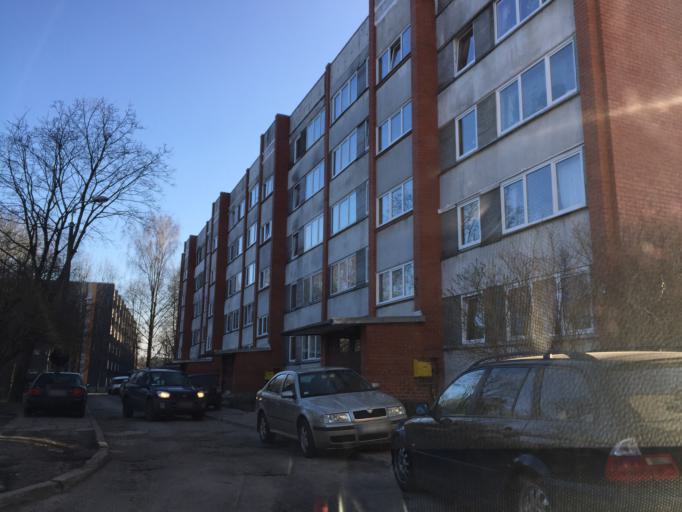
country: LV
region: Riga
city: Bergi
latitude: 56.9772
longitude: 24.2640
